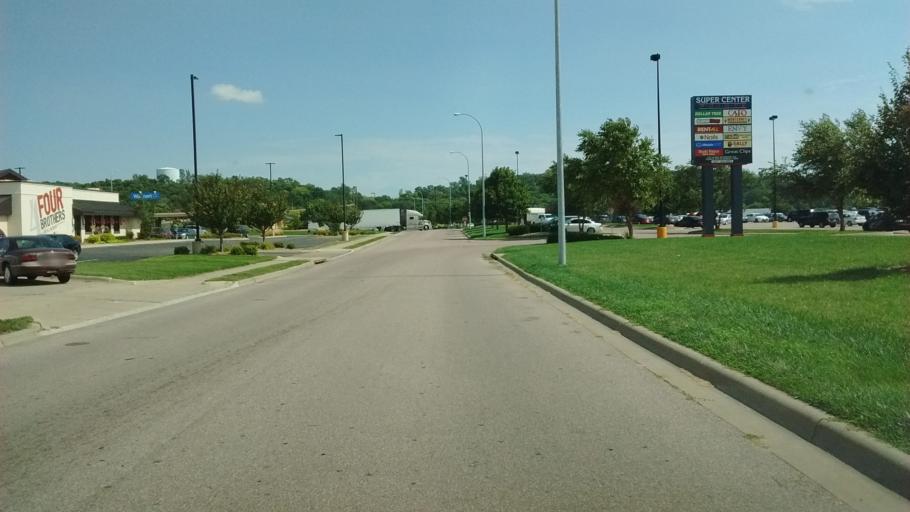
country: US
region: Iowa
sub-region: Woodbury County
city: Sergeant Bluff
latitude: 42.4350
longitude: -96.3659
